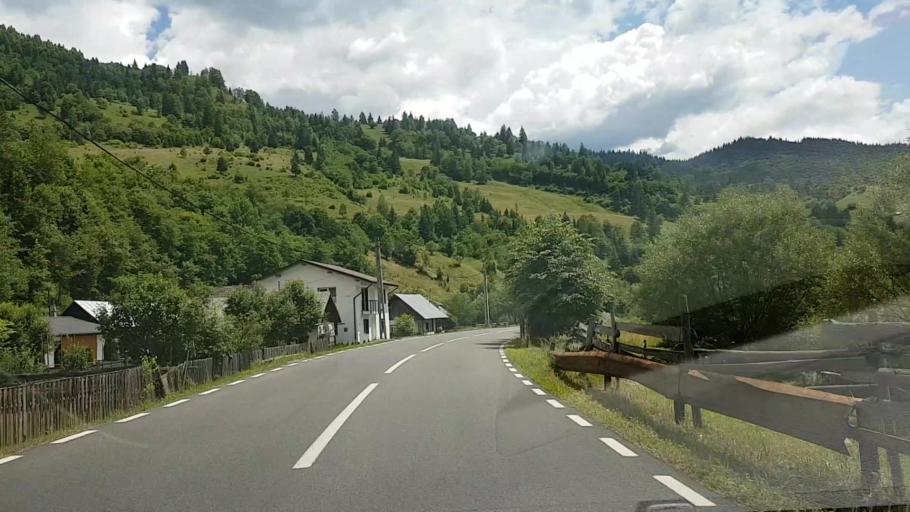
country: RO
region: Suceava
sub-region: Comuna Crucea
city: Crucea
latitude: 47.3912
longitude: 25.5771
